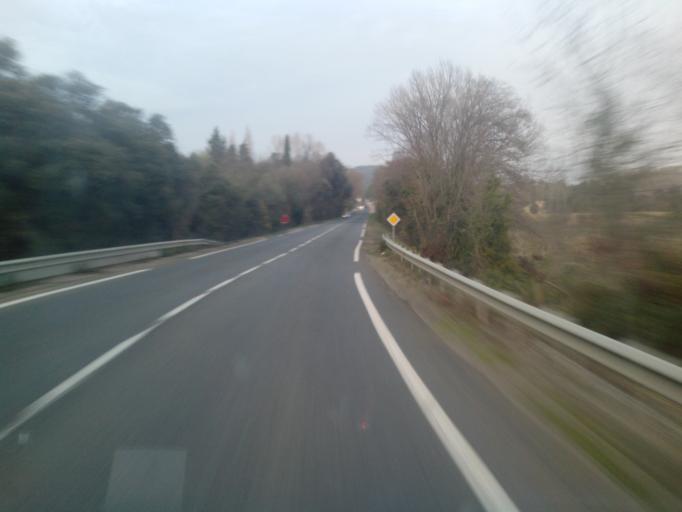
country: FR
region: Languedoc-Roussillon
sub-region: Departement de l'Aude
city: Bize-Minervois
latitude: 43.2936
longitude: 2.8676
